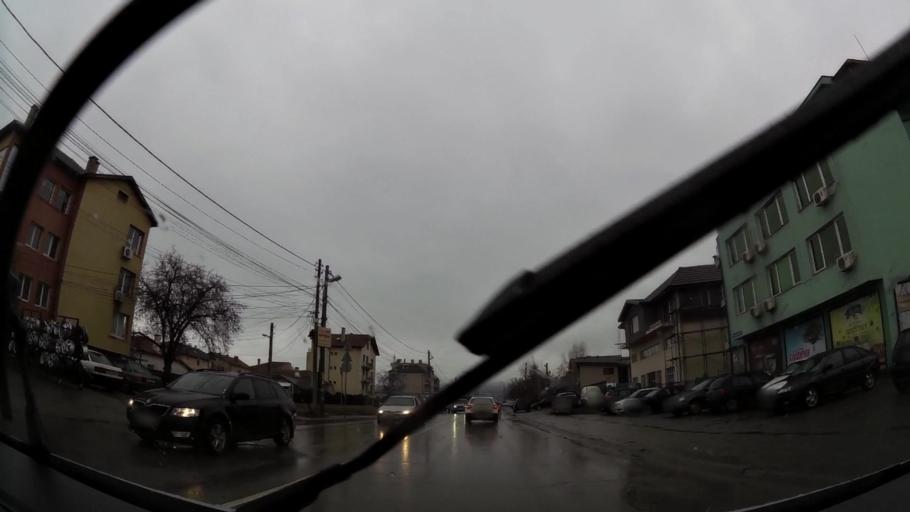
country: BG
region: Sofia-Capital
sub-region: Stolichna Obshtina
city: Sofia
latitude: 42.6249
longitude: 23.4062
